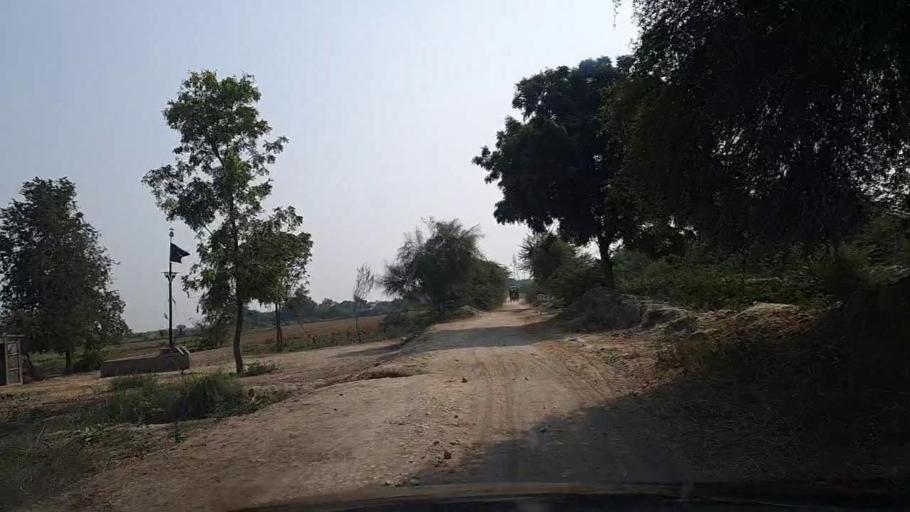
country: PK
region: Sindh
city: Mirpur Batoro
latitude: 24.7049
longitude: 68.2164
